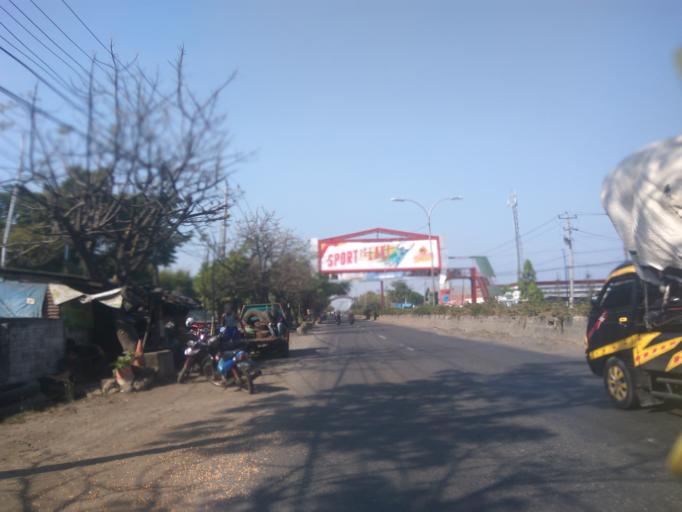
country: ID
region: Central Java
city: Semarang
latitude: -6.9480
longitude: 110.4898
